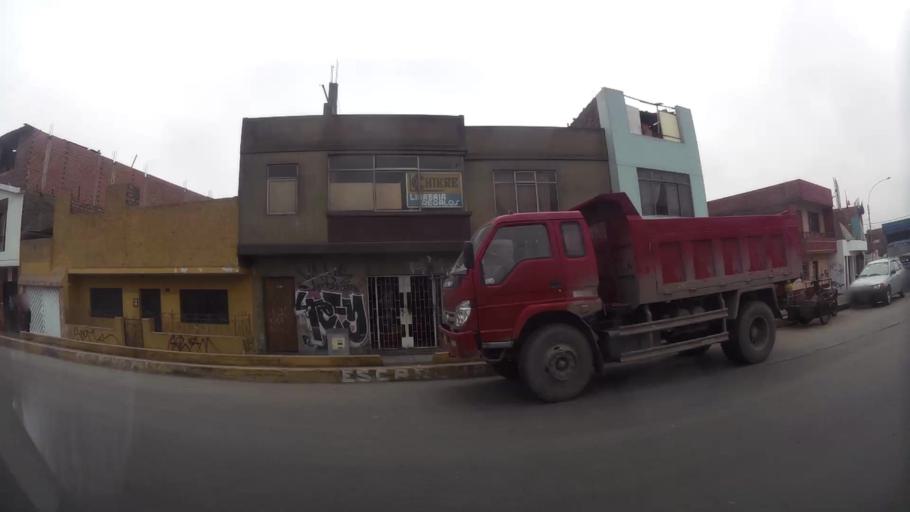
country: PE
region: Lima
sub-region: Lima
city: Independencia
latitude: -12.0268
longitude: -77.0757
